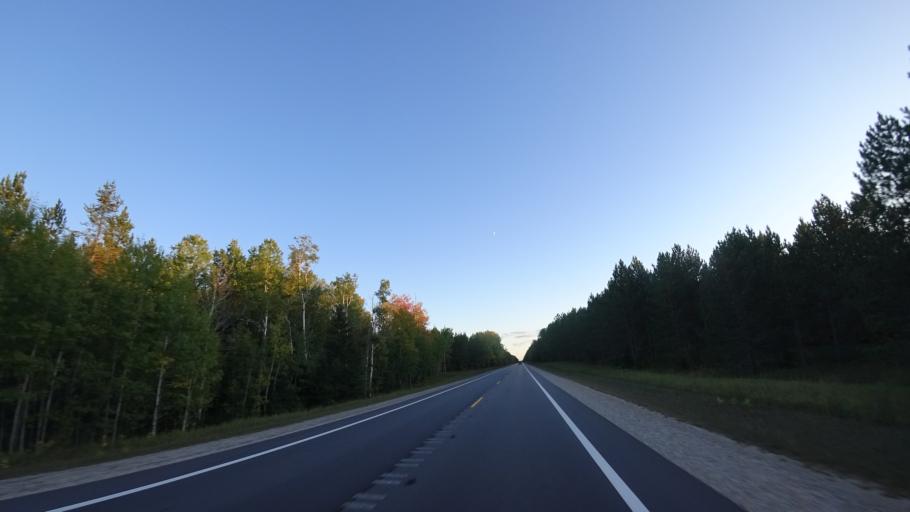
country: US
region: Michigan
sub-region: Luce County
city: Newberry
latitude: 46.3083
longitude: -85.0094
